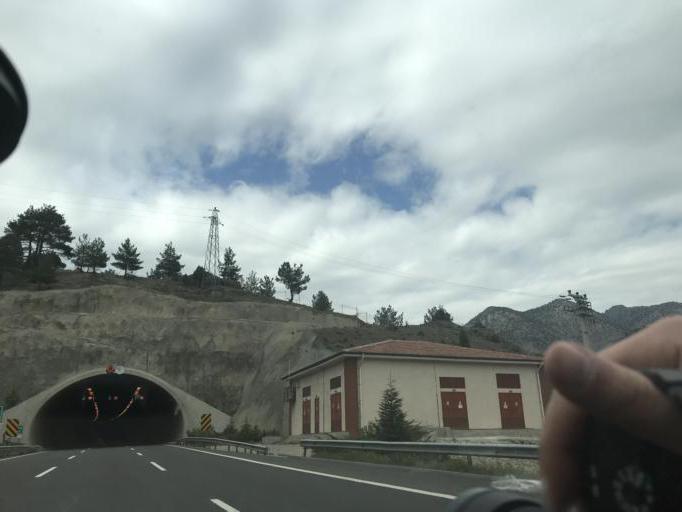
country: TR
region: Nigde
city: Ciftehan
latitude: 37.5210
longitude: 34.8177
